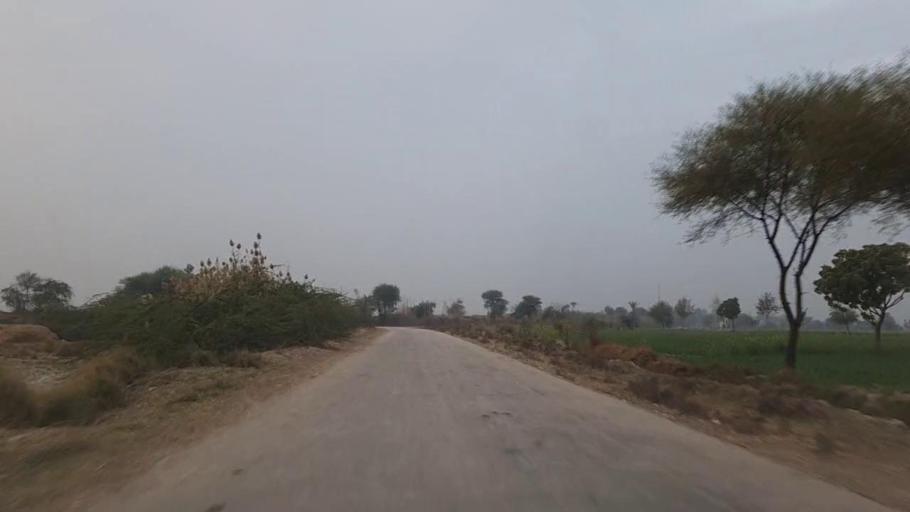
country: PK
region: Sindh
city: Jam Sahib
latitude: 26.3237
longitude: 68.5445
